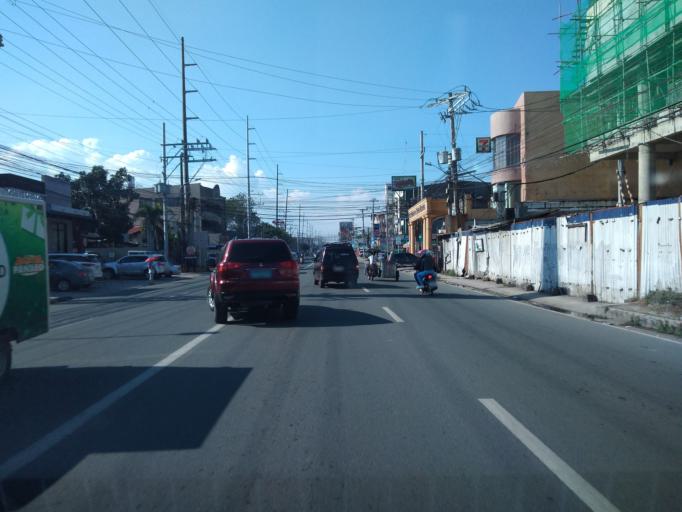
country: PH
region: Calabarzon
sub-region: Province of Laguna
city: Calamba
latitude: 14.1938
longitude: 121.1653
